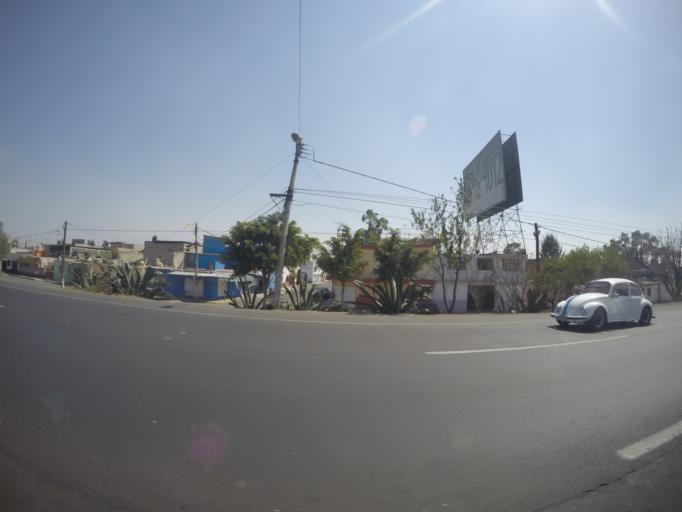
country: MX
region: Mexico
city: Ecatepec
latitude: 19.6036
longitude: -99.0333
